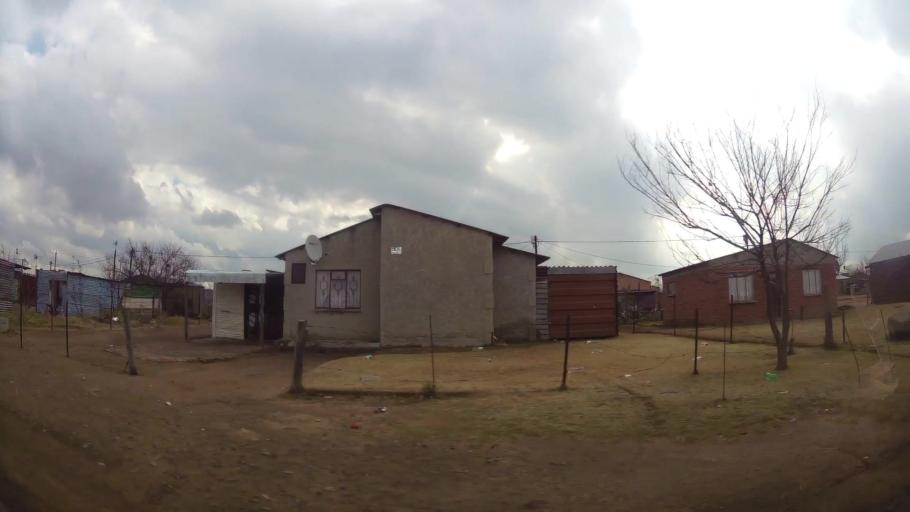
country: ZA
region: Orange Free State
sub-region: Fezile Dabi District Municipality
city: Sasolburg
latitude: -26.8617
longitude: 27.9018
